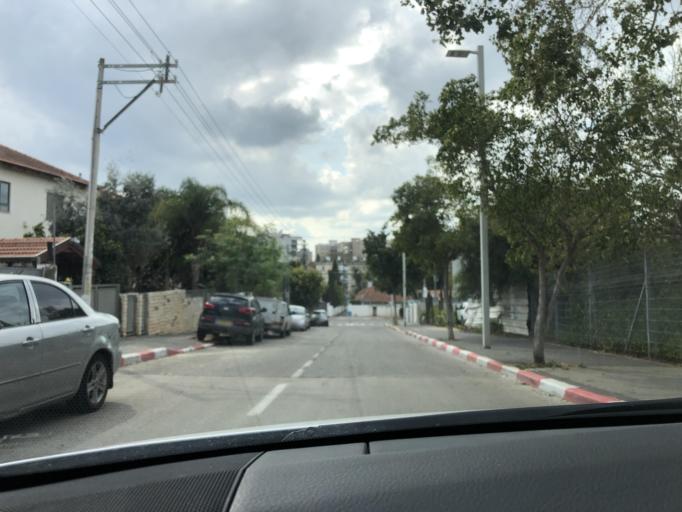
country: IL
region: Central District
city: Ganne Tiqwa
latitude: 32.0591
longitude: 34.8720
